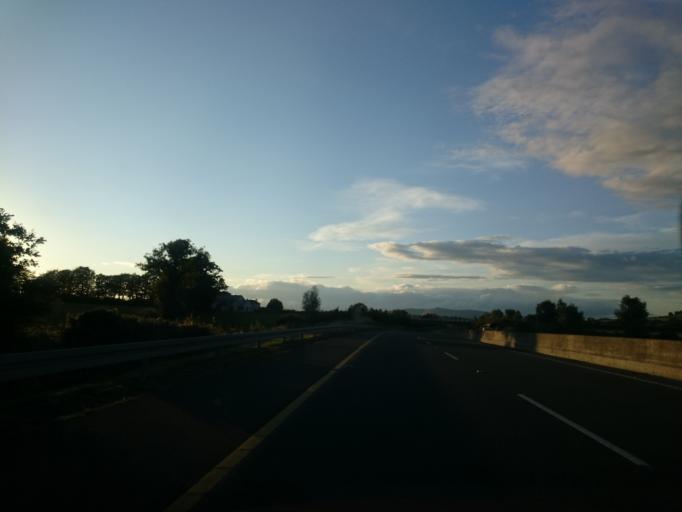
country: IE
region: Leinster
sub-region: Loch Garman
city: Gorey
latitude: 52.6835
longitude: -6.2620
